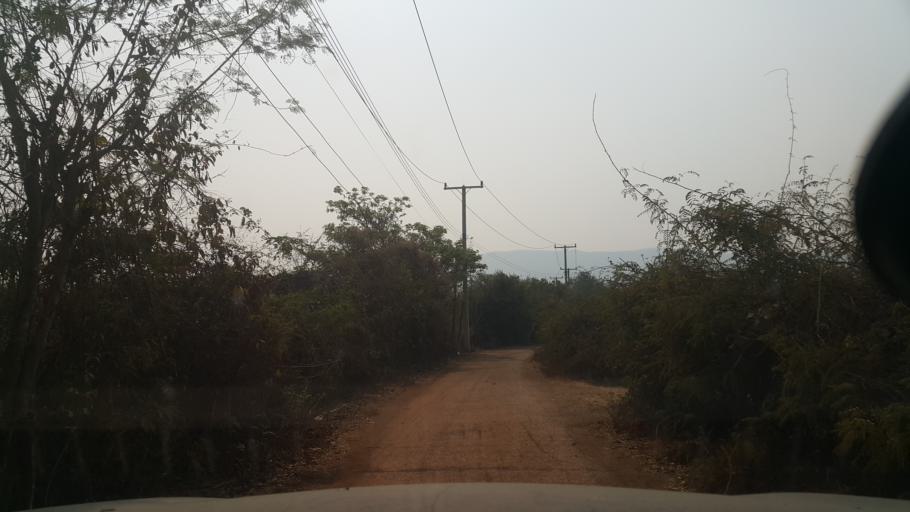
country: TH
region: Chiang Mai
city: Mae On
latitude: 18.7616
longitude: 99.2632
